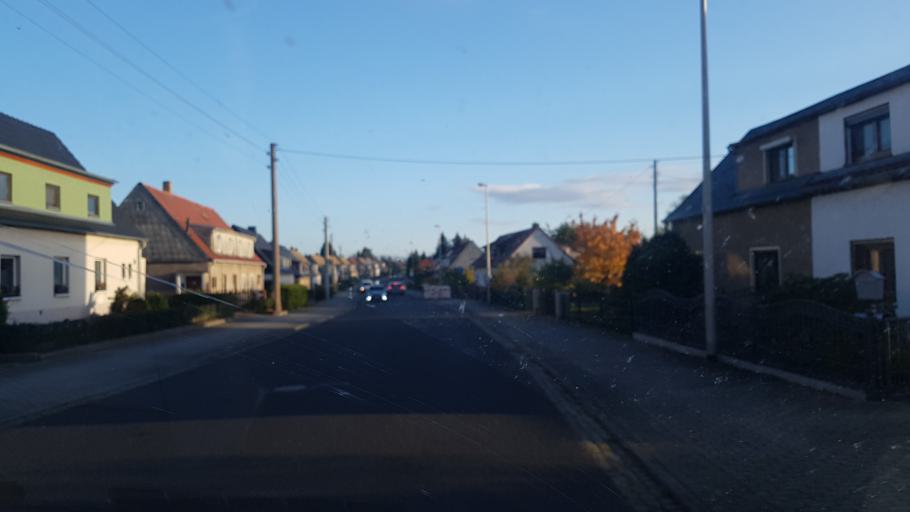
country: DE
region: Saxony
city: Oschatz
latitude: 51.3113
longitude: 13.0936
